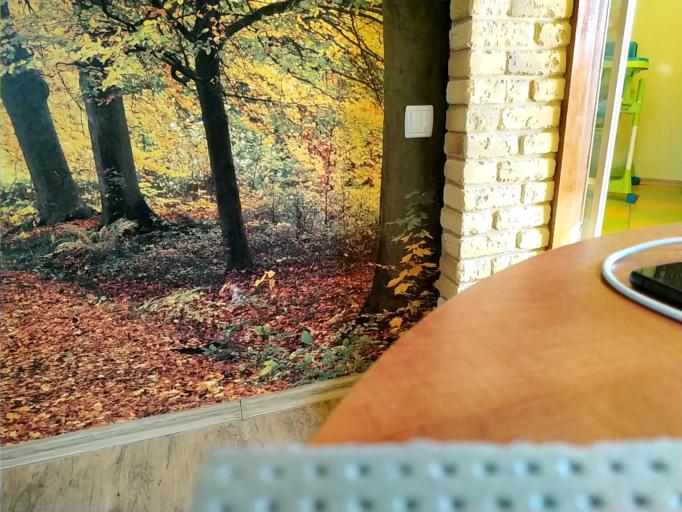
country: RU
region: Tverskaya
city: Kalashnikovo
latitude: 57.3466
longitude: 35.2179
